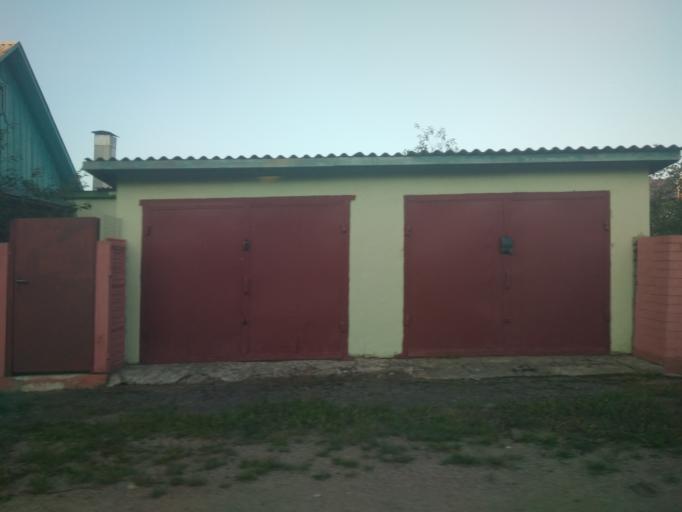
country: BY
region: Minsk
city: Minsk
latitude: 53.9393
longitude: 27.5592
